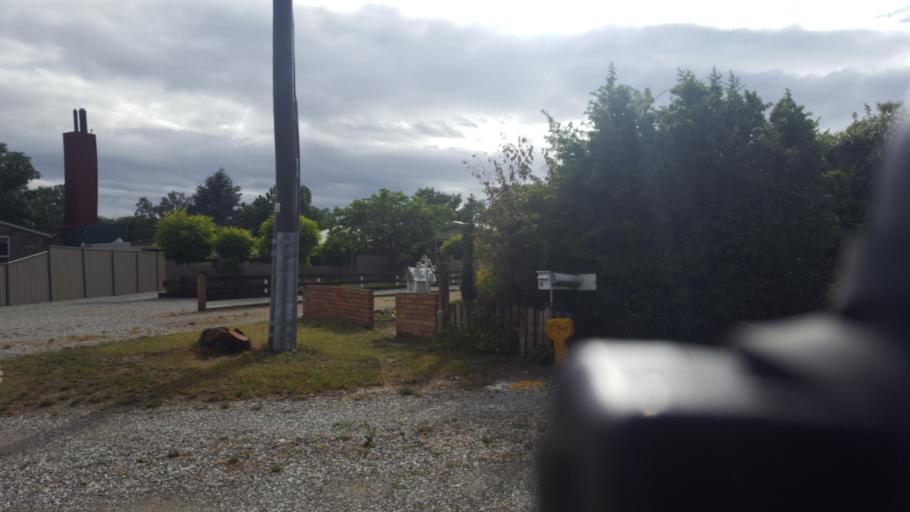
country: NZ
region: Otago
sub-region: Queenstown-Lakes District
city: Wanaka
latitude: -45.2460
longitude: 169.3852
